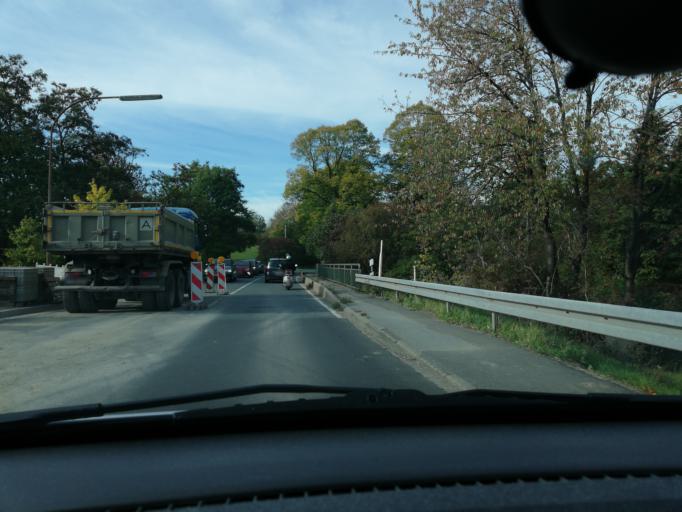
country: DE
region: North Rhine-Westphalia
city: Sprockhovel
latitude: 51.3323
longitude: 7.2622
